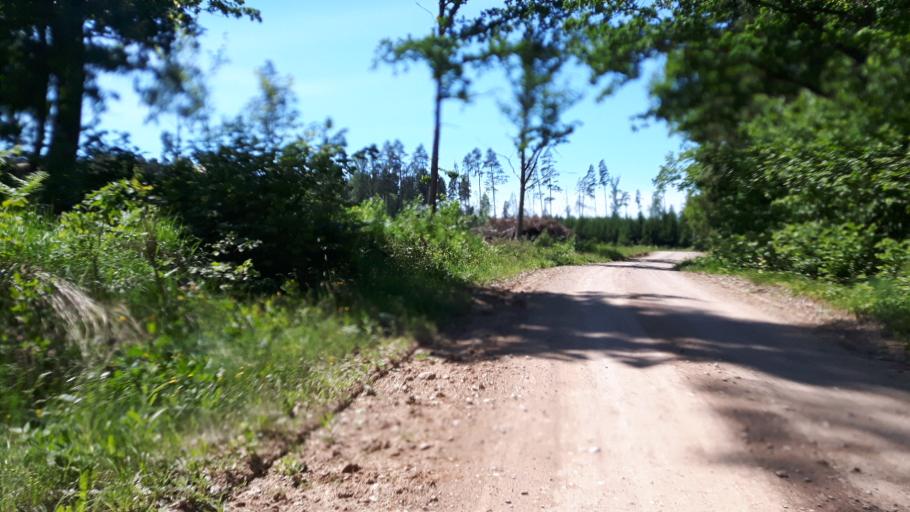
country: LV
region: Kandava
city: Kandava
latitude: 57.0420
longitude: 22.8399
